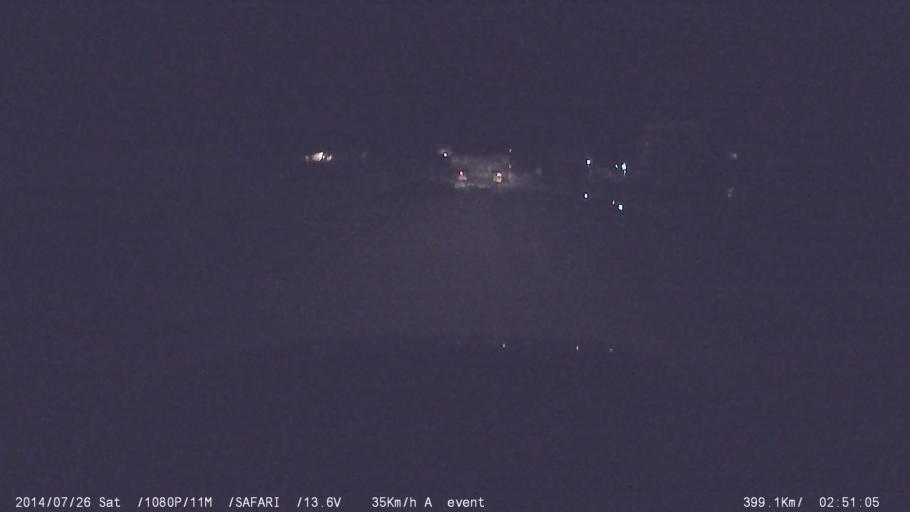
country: IN
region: Kerala
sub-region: Palakkad district
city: Palakkad
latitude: 10.7501
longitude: 76.6615
